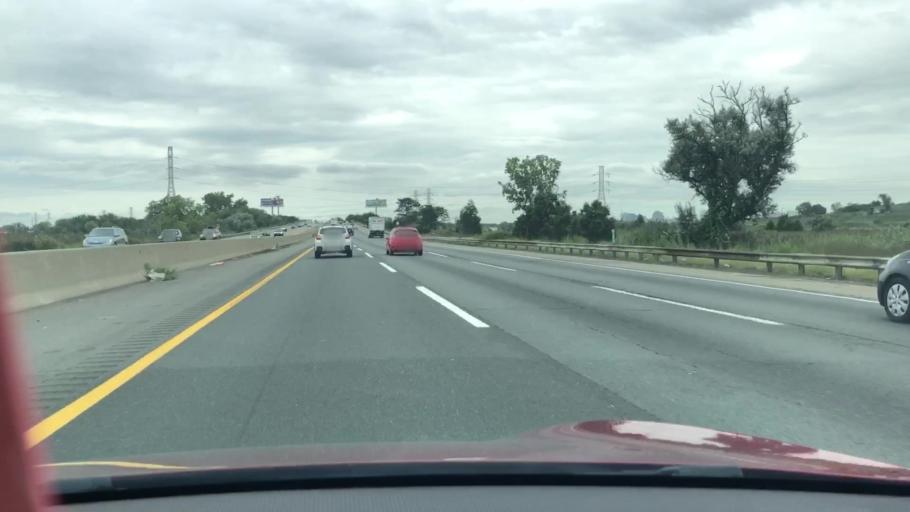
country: US
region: New Jersey
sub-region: Bergen County
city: North Arlington
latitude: 40.7669
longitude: -74.1101
